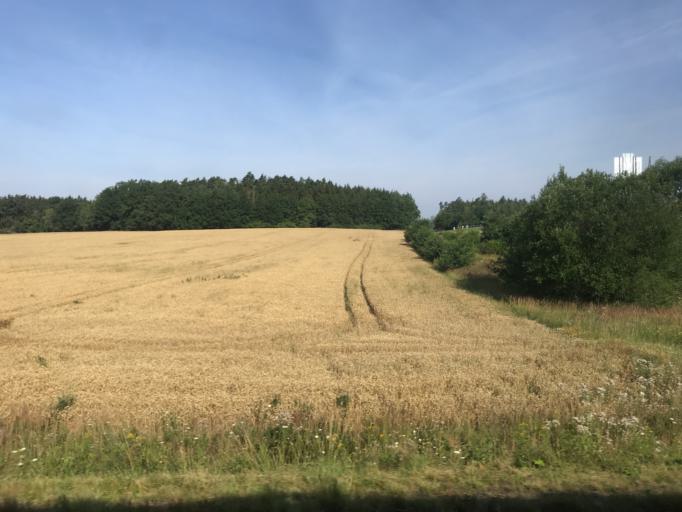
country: CZ
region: Jihocesky
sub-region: Okres Tabor
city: Tabor
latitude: 49.4368
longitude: 14.6887
